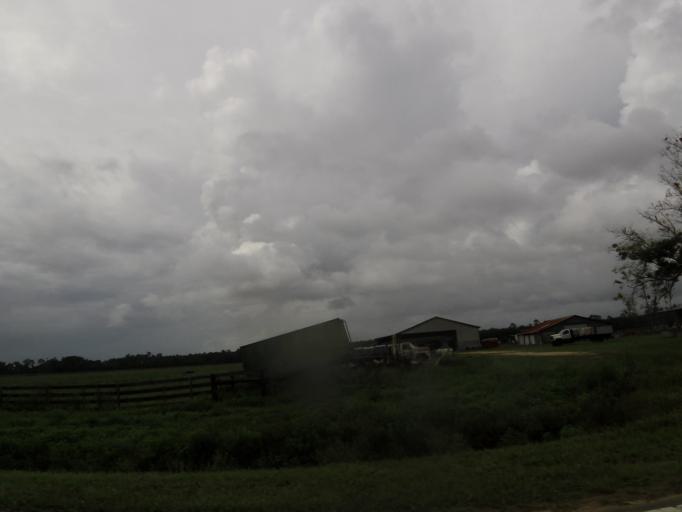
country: US
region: Florida
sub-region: Saint Johns County
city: Saint Augustine South
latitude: 29.8512
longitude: -81.5018
